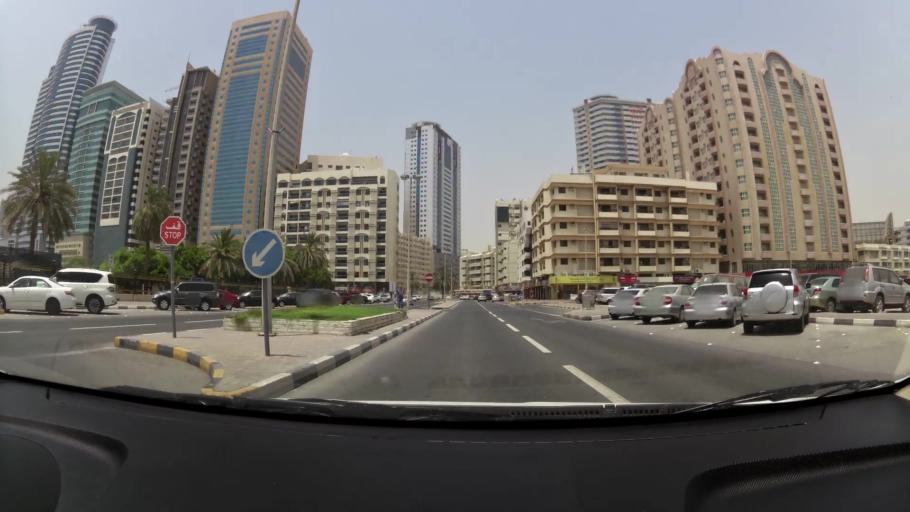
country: AE
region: Ash Shariqah
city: Sharjah
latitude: 25.3273
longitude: 55.3921
